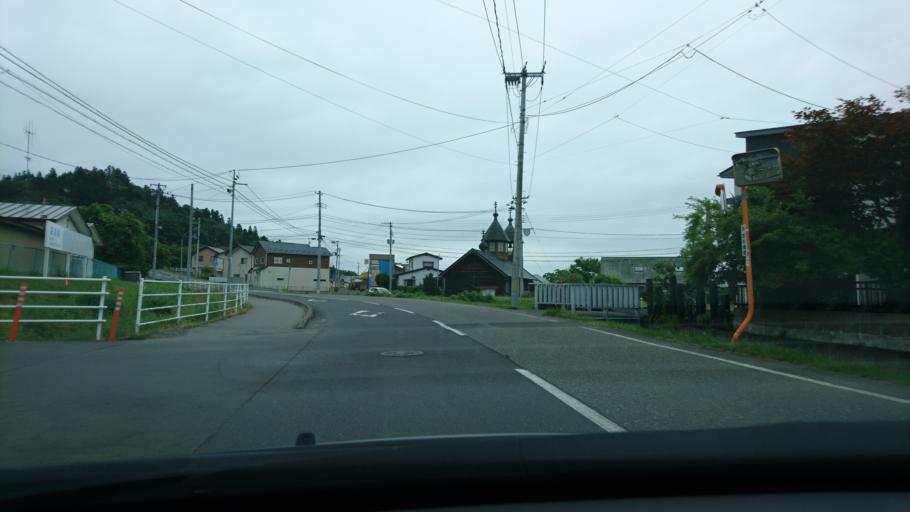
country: JP
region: Iwate
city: Ichinoseki
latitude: 38.9228
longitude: 141.1224
